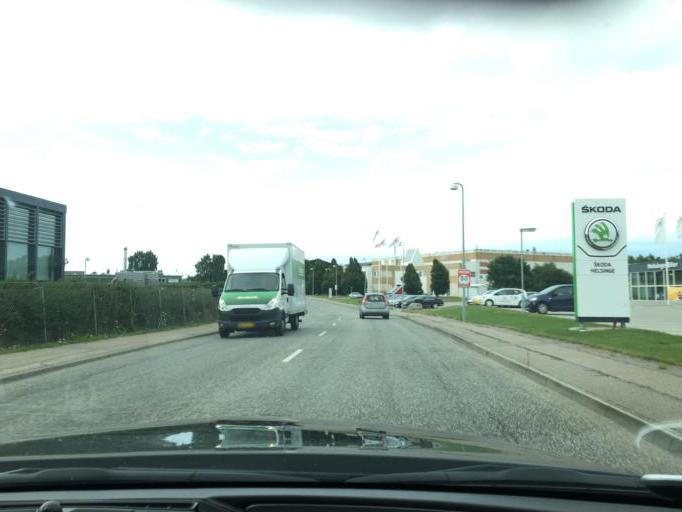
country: DK
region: Capital Region
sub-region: Gribskov Kommune
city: Helsinge
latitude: 56.0124
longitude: 12.1995
